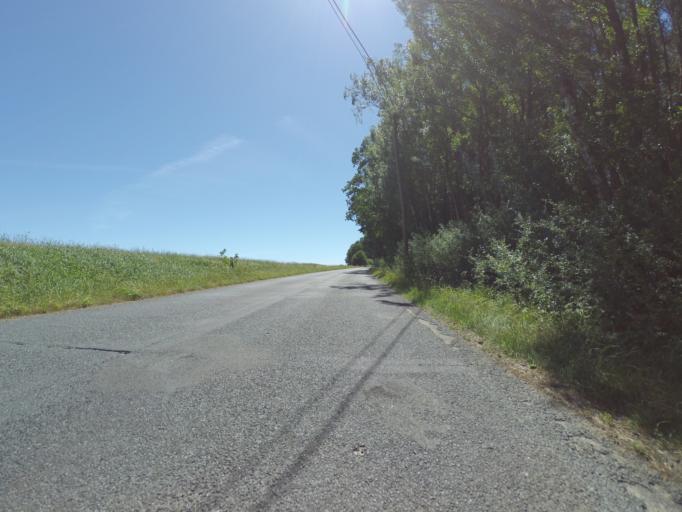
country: DE
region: Mecklenburg-Vorpommern
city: Plau am See
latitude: 53.4209
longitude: 12.3250
